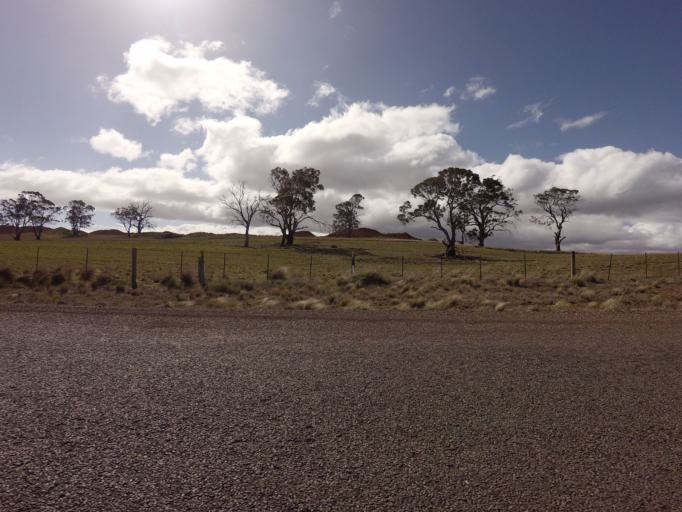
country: AU
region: Tasmania
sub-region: Northern Midlands
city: Evandale
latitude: -41.9064
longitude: 147.4565
